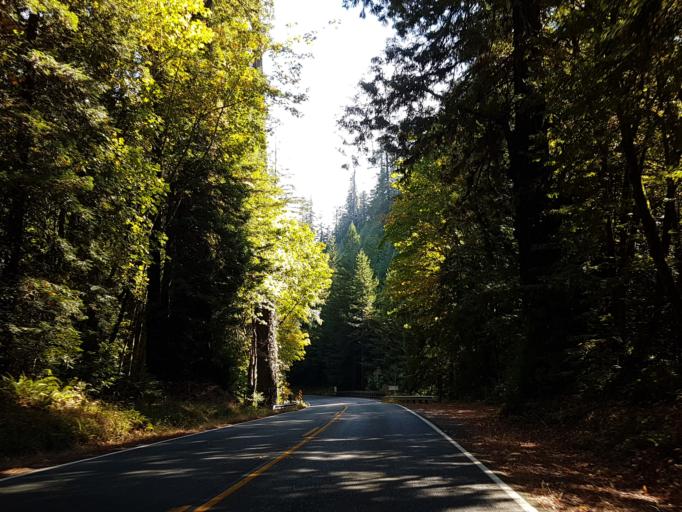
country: US
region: California
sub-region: Humboldt County
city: Rio Dell
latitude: 40.4322
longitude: -123.9849
